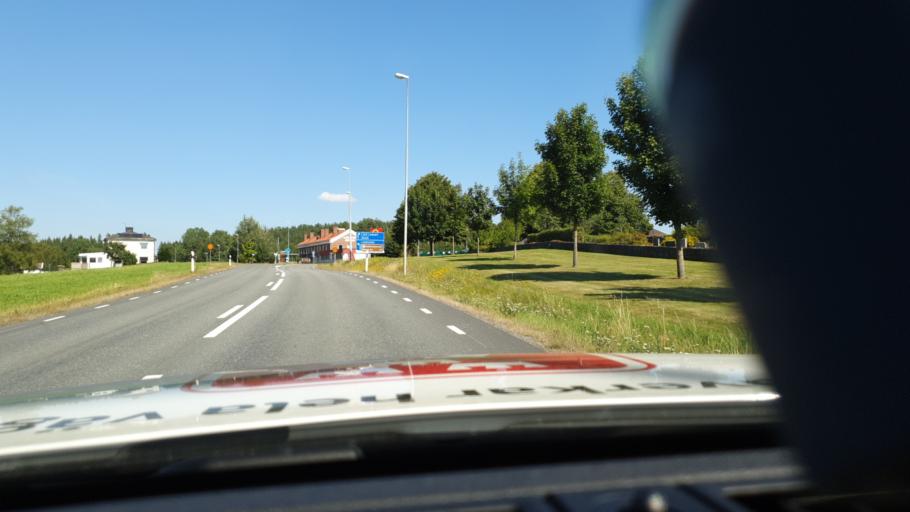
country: SE
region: Joenkoeping
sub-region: Jonkopings Kommun
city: Tenhult
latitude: 57.7725
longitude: 14.4159
